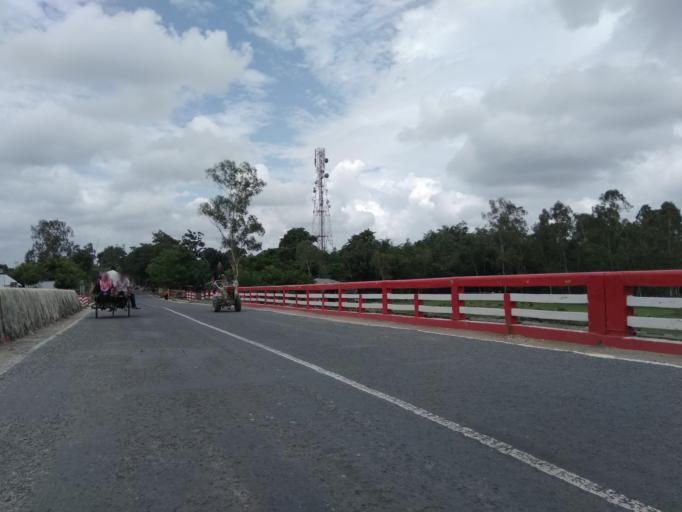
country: BD
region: Rajshahi
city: Saidpur
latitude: 25.7735
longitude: 88.7934
